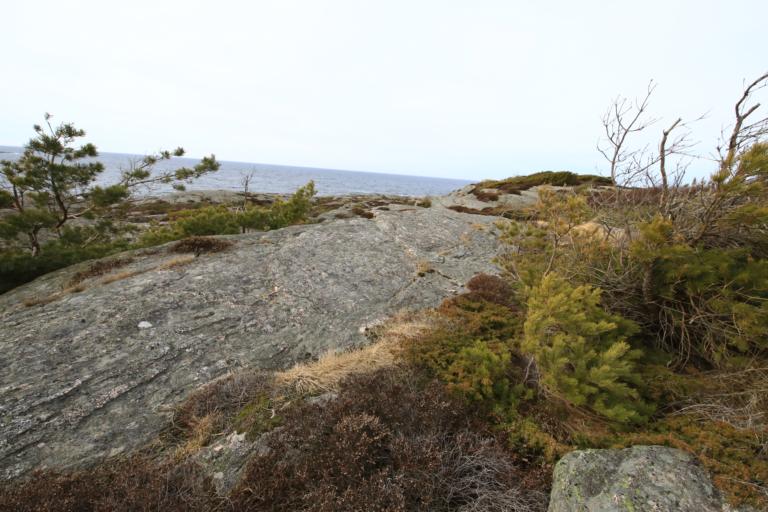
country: SE
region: Halland
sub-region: Kungsbacka Kommun
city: Frillesas
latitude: 57.2328
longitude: 12.0997
